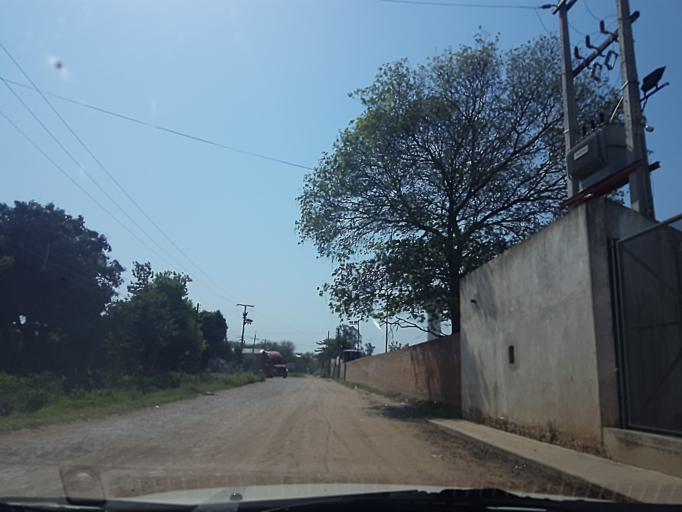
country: PY
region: Central
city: Colonia Mariano Roque Alonso
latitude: -25.2045
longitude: -57.5321
